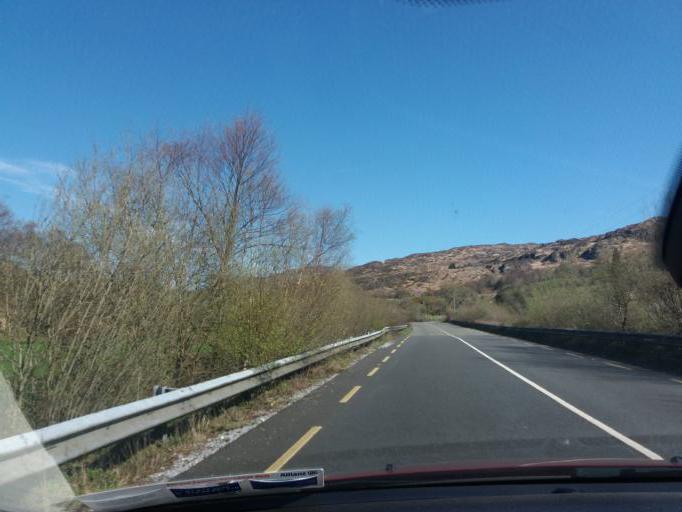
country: IE
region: Munster
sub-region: Ciarrai
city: Cill Airne
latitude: 51.9367
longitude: -9.3822
